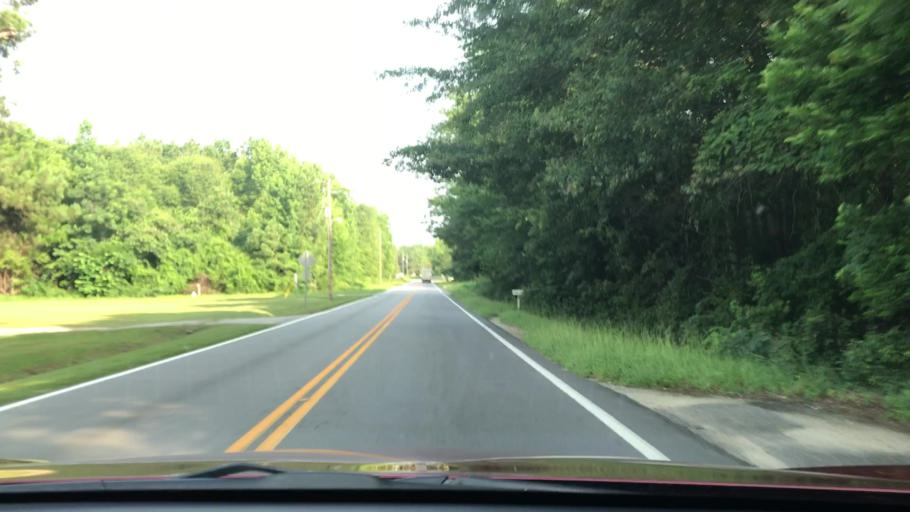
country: US
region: South Carolina
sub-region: Bamberg County
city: Denmark
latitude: 33.5331
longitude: -81.1280
